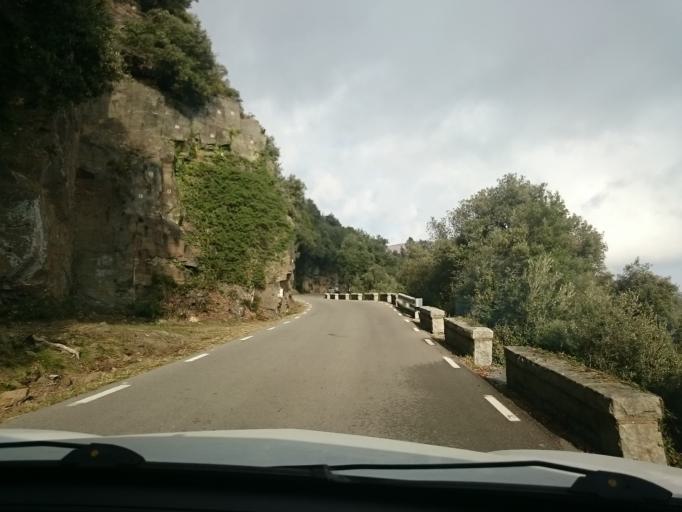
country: ES
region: Catalonia
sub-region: Provincia de Barcelona
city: Fogars de Montclus
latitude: 41.7516
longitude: 2.4756
